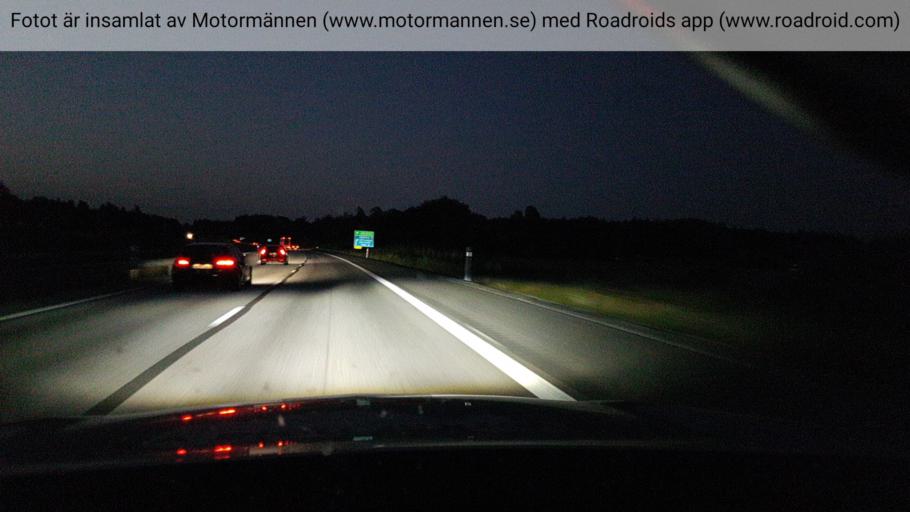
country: SE
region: OErebro
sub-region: Lindesbergs Kommun
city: Fellingsbro
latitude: 59.3342
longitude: 15.5283
